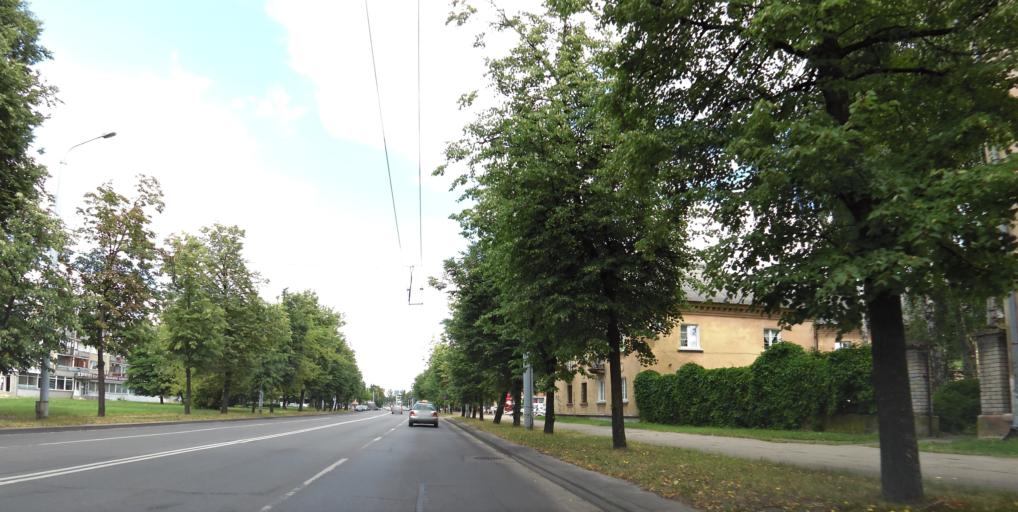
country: LT
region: Vilnius County
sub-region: Vilnius
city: Vilnius
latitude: 54.7095
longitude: 25.2859
